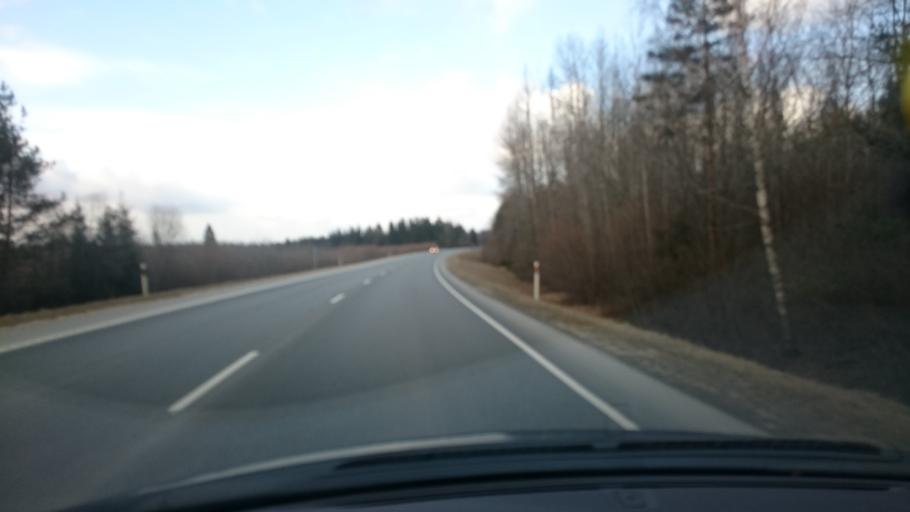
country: EE
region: Harju
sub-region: Nissi vald
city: Turba
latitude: 59.1065
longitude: 24.2539
